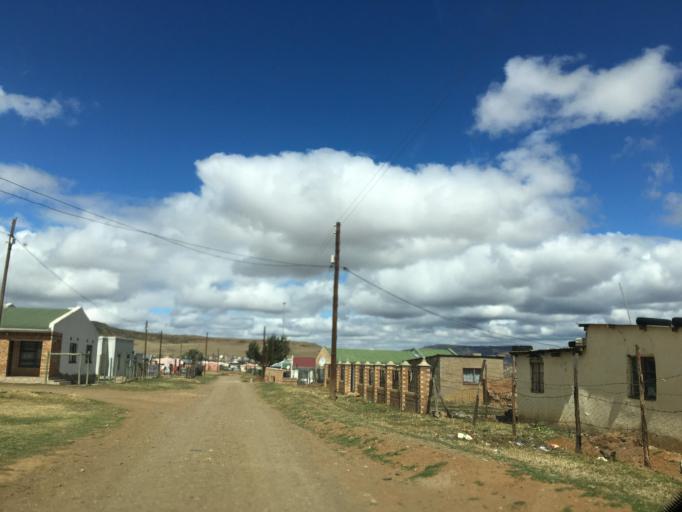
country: ZA
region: Eastern Cape
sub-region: Chris Hani District Municipality
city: Cala
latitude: -31.5329
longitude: 27.7026
